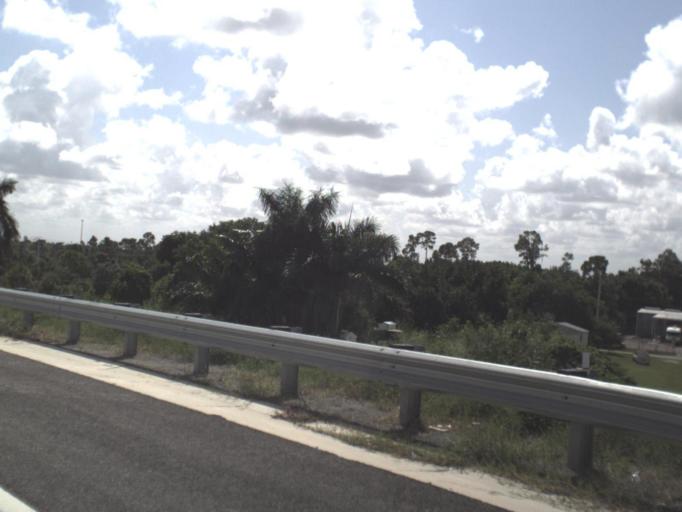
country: US
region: Florida
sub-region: Charlotte County
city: Punta Gorda
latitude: 26.9387
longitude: -82.0258
